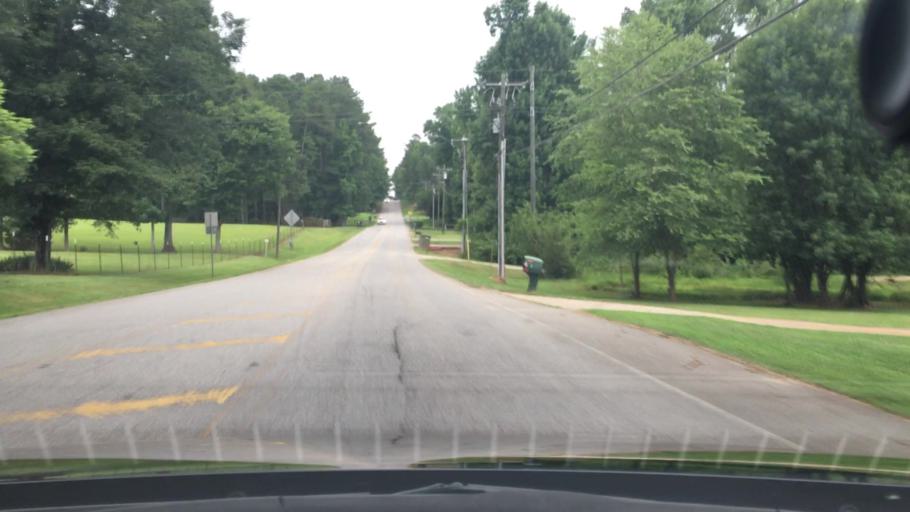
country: US
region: Georgia
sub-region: Coweta County
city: East Newnan
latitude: 33.3562
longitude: -84.7124
